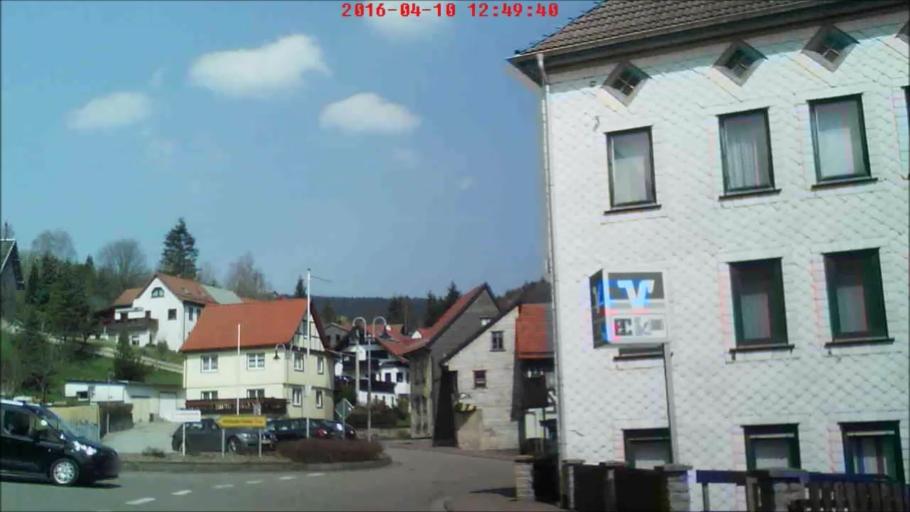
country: DE
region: Thuringia
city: Pappenheim
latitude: 50.7962
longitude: 10.4750
